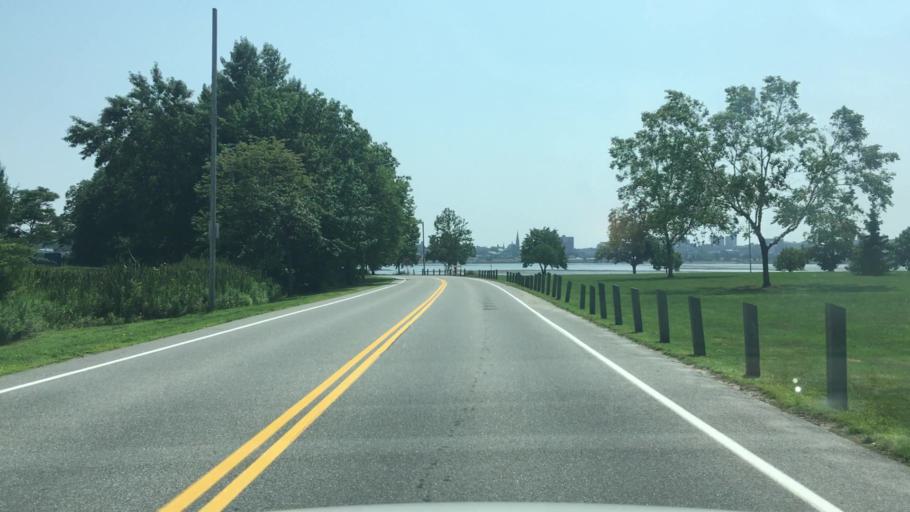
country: US
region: Maine
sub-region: Cumberland County
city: Portland
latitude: 43.6805
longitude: -70.2666
